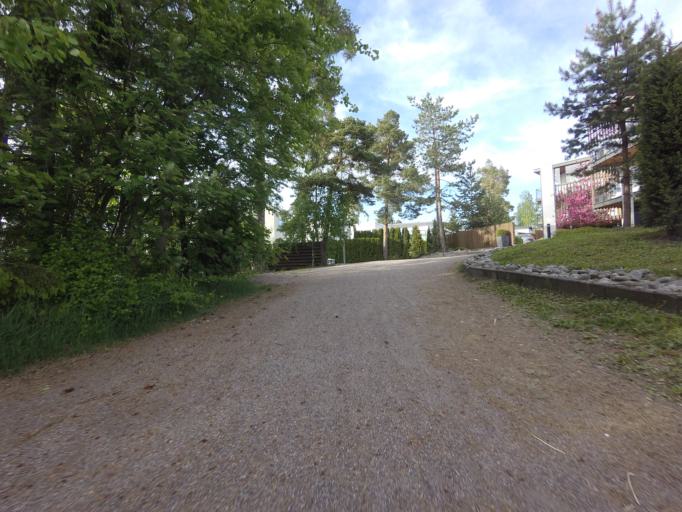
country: FI
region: Uusimaa
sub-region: Helsinki
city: Koukkuniemi
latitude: 60.1457
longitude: 24.7338
